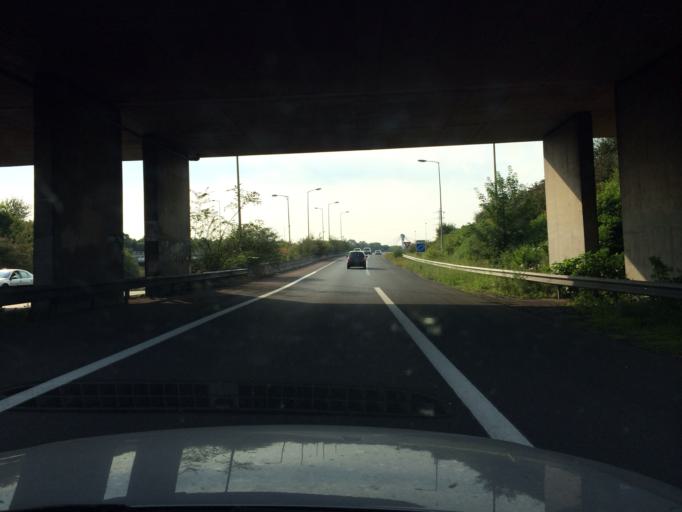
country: FR
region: Lower Normandy
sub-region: Departement du Calvados
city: Giberville
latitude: 49.1692
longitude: -0.3007
